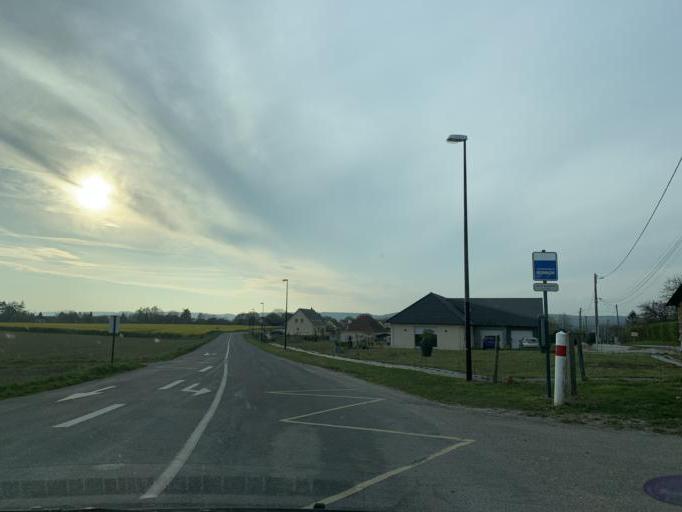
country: FR
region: Haute-Normandie
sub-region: Departement de la Seine-Maritime
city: Saint-Wandrille-Rancon
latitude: 49.5031
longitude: 0.7479
